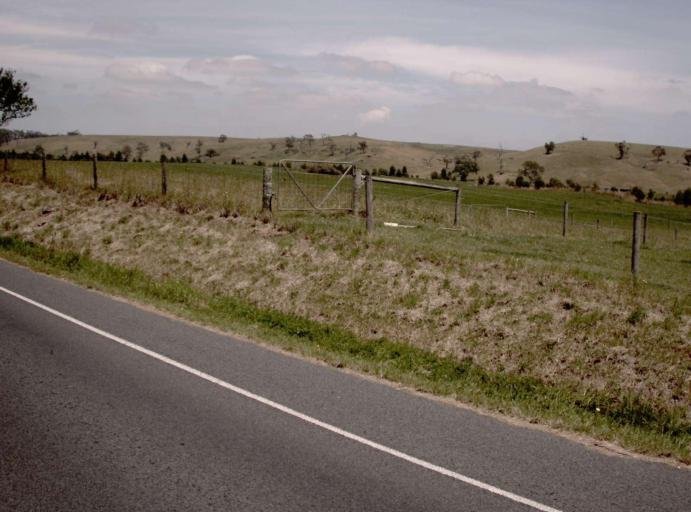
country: AU
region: Victoria
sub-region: Latrobe
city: Traralgon
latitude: -38.2236
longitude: 146.5443
